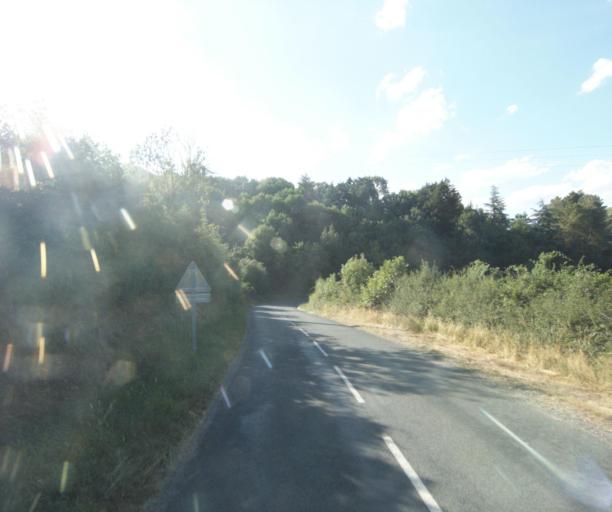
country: FR
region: Rhone-Alpes
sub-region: Departement du Rhone
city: Lentilly
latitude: 45.8012
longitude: 4.6603
